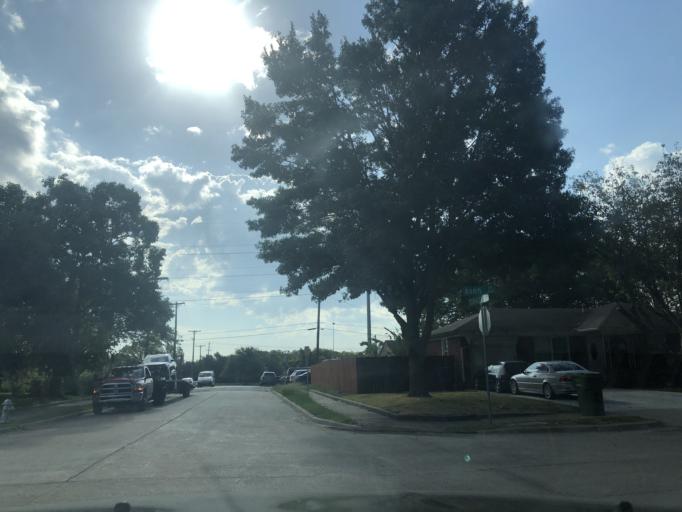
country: US
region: Texas
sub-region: Dallas County
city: Garland
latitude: 32.8876
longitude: -96.6557
